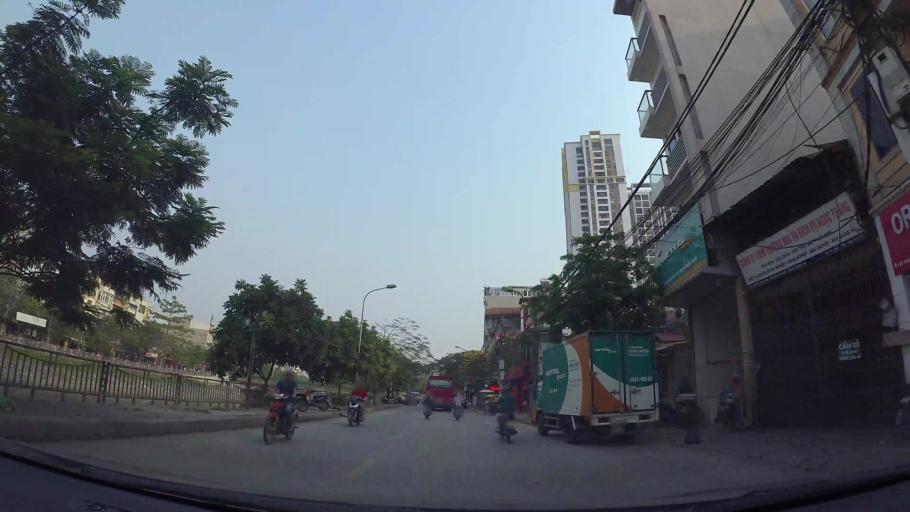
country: VN
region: Ha Noi
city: Thanh Xuan
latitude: 20.9872
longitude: 105.8131
